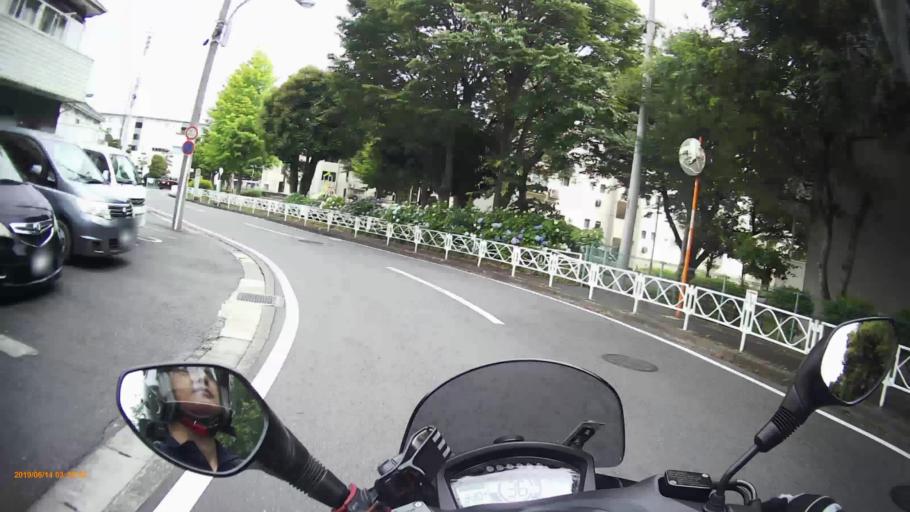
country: JP
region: Kanagawa
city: Minami-rinkan
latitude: 35.4141
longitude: 139.4497
